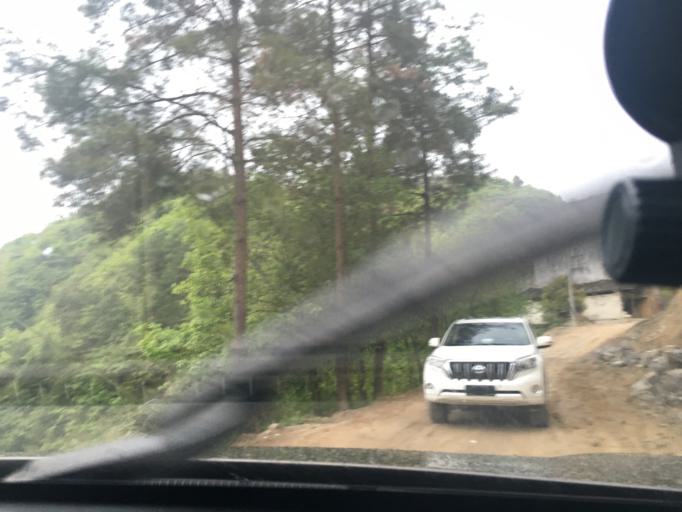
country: CN
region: Guizhou Sheng
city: Changbao
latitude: 28.2093
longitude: 108.2842
